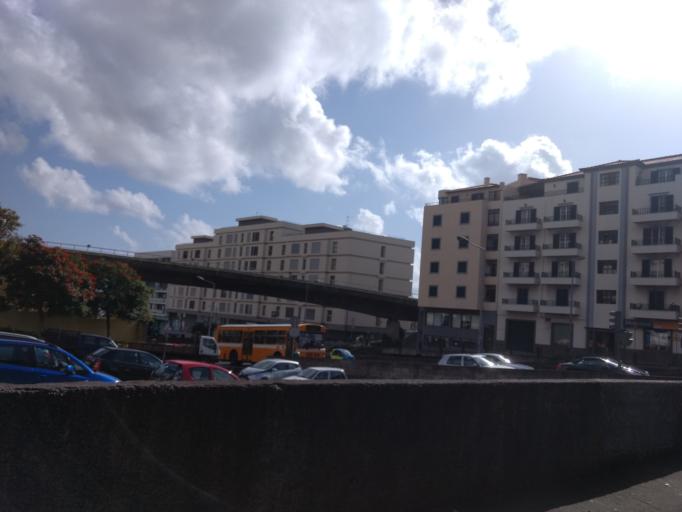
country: PT
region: Madeira
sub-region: Funchal
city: Nossa Senhora do Monte
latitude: 32.6532
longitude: -16.9110
